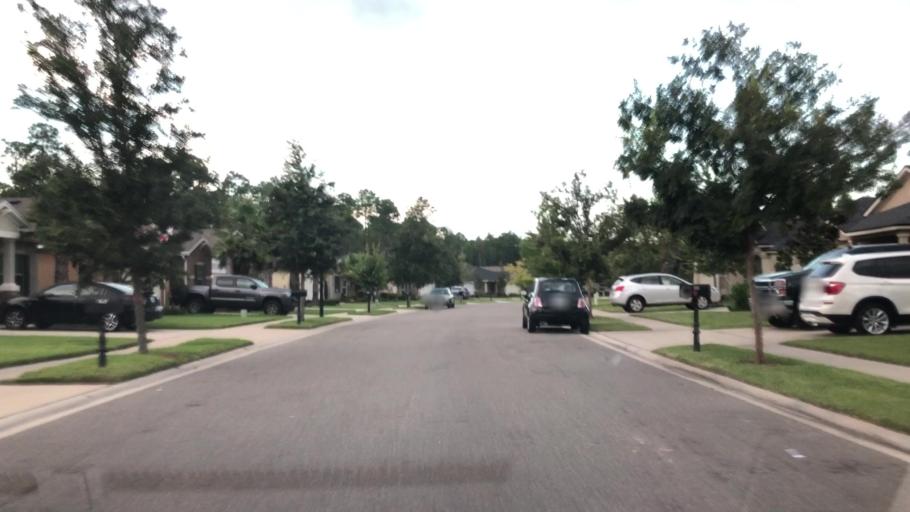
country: US
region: Florida
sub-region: Saint Johns County
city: Palm Valley
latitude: 30.1180
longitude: -81.4464
